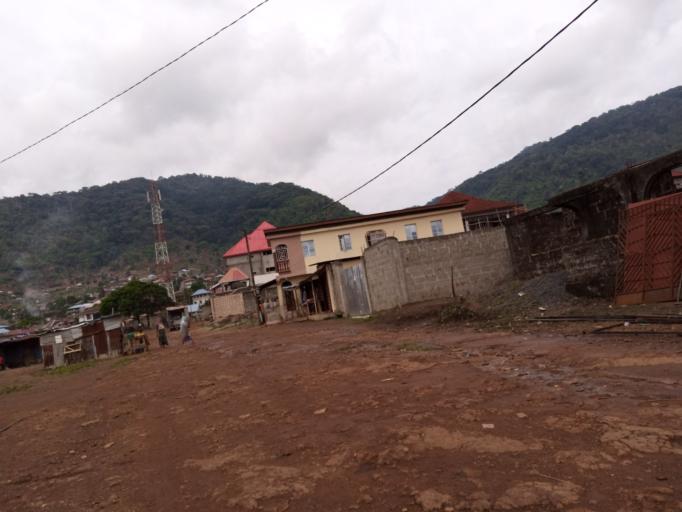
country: SL
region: Western Area
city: Hastings
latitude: 8.3785
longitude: -13.1534
